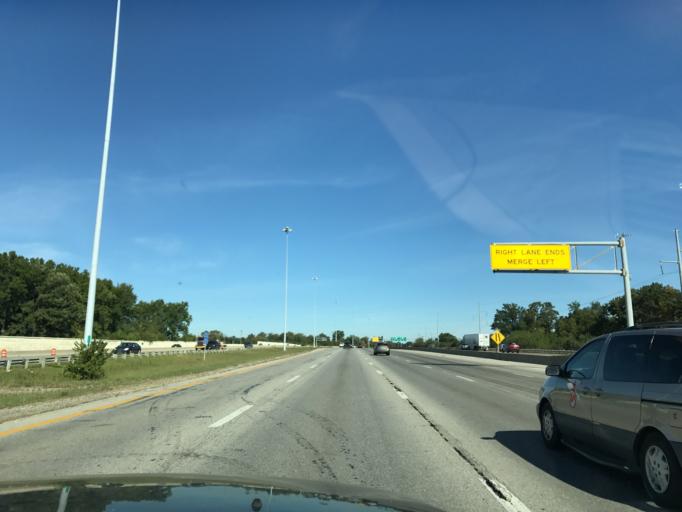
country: US
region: Ohio
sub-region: Franklin County
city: Huber Ridge
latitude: 40.0662
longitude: -82.9062
